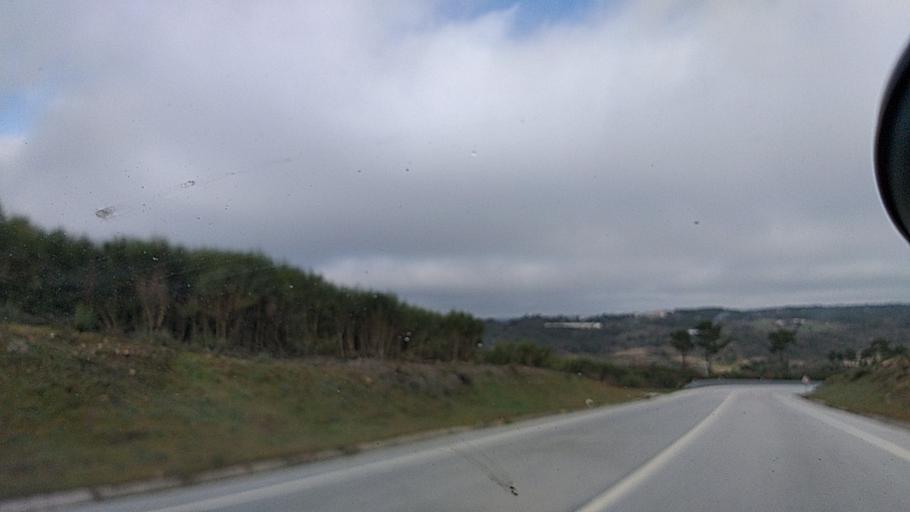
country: PT
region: Guarda
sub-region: Aguiar da Beira
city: Aguiar da Beira
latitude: 40.7712
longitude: -7.5036
